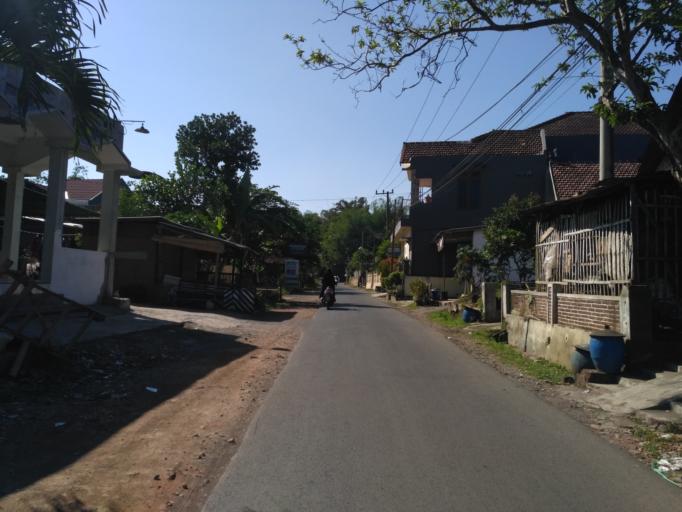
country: ID
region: East Java
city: Singosari
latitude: -7.9173
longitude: 112.6654
